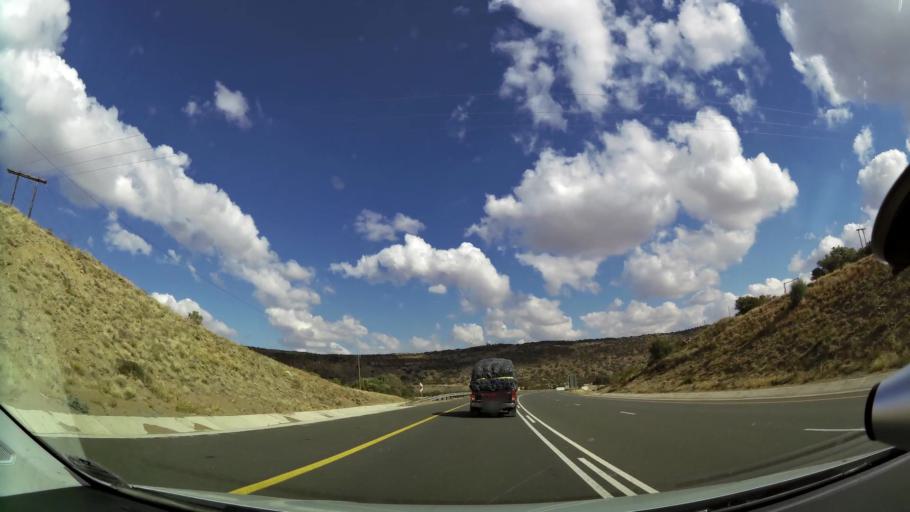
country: ZA
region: Orange Free State
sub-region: Mangaung Metropolitan Municipality
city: Bloemfontein
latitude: -29.1561
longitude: 26.0575
